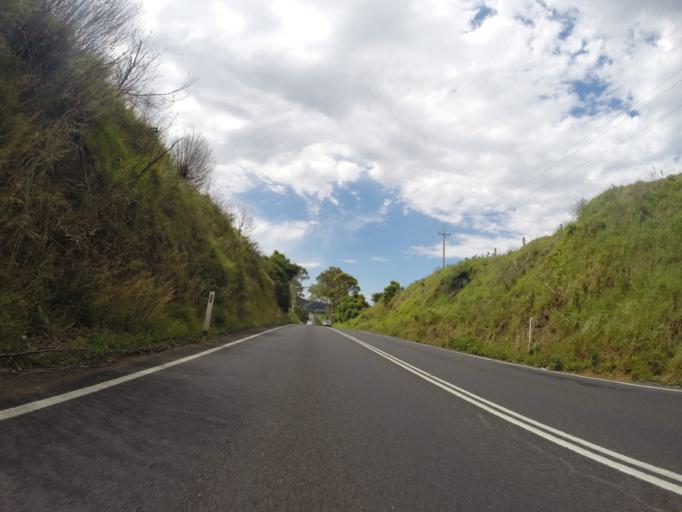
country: AU
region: New South Wales
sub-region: Shoalhaven Shire
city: Milton
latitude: -35.2875
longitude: 150.4212
